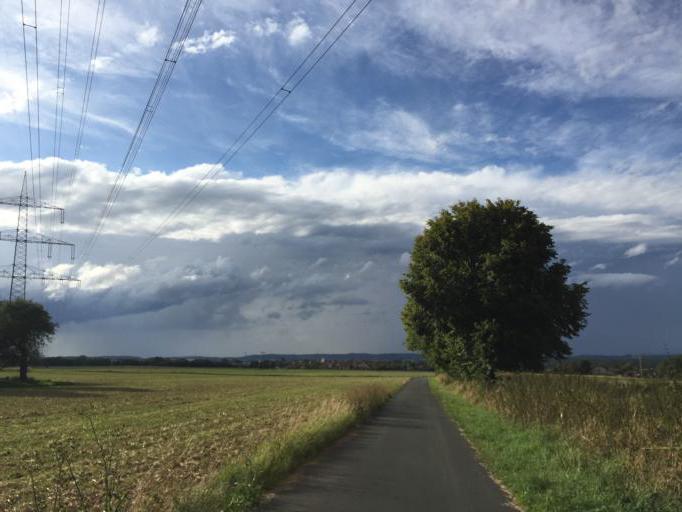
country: DE
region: Hesse
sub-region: Regierungsbezirk Giessen
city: Langgons
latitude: 50.5152
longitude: 8.6786
